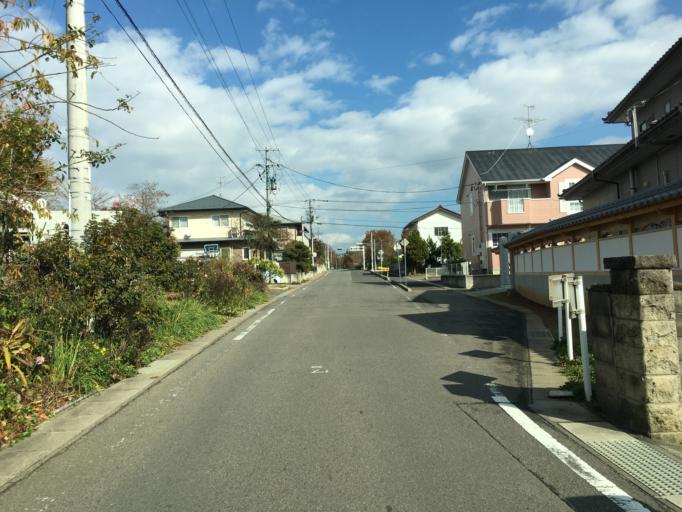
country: JP
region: Fukushima
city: Nihommatsu
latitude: 37.6514
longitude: 140.4865
